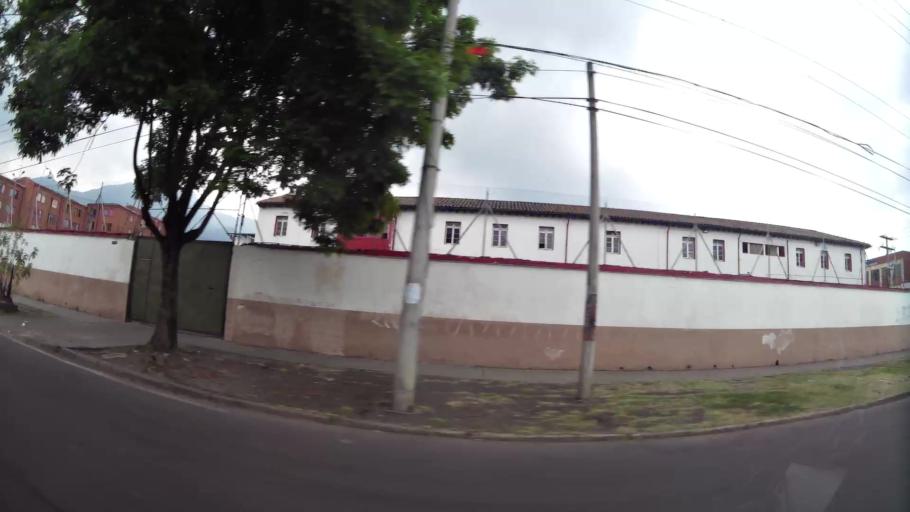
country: CO
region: Bogota D.C.
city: Bogota
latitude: 4.5804
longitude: -74.0886
